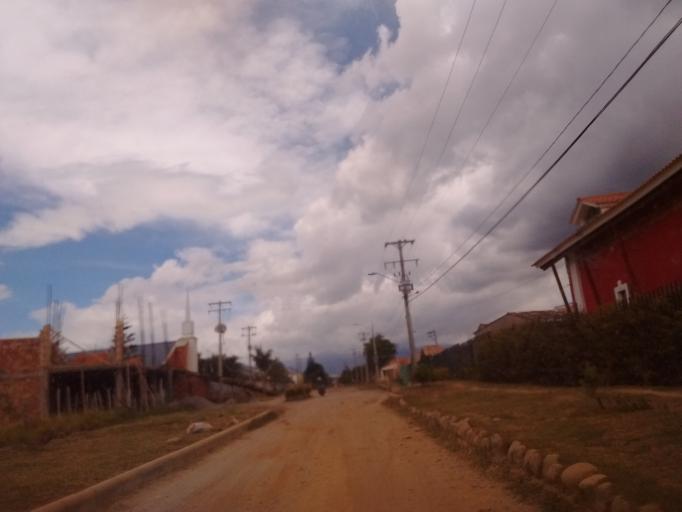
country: CO
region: Cauca
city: Popayan
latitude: 2.4946
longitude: -76.5661
